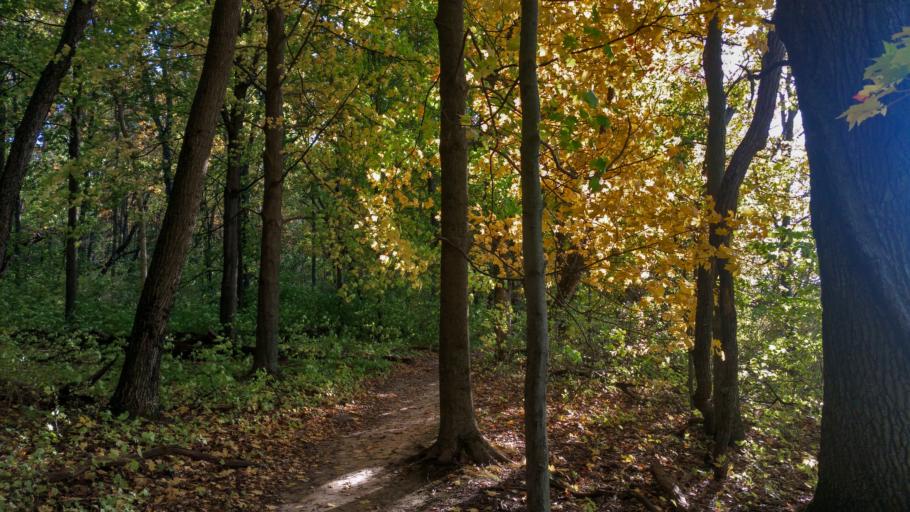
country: US
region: Wisconsin
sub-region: Dane County
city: Shorewood Hills
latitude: 43.0467
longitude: -89.4291
